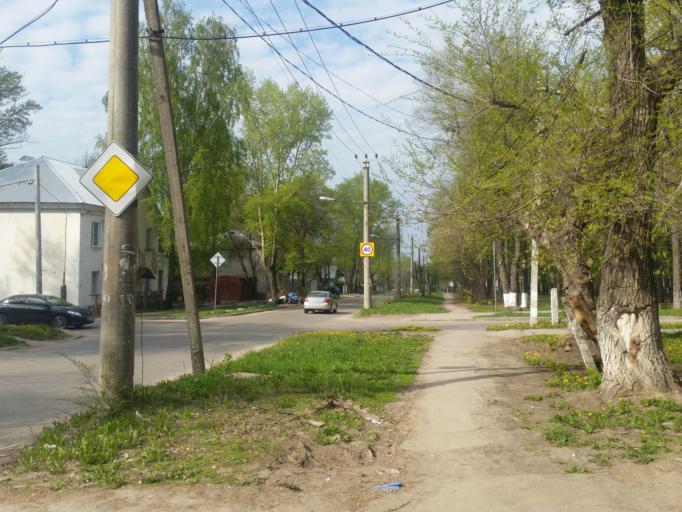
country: RU
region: Ulyanovsk
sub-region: Ulyanovskiy Rayon
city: Ulyanovsk
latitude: 54.3394
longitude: 48.3783
